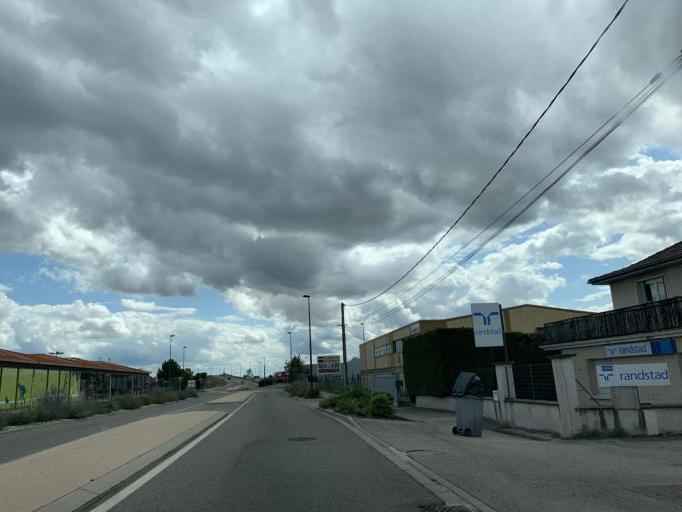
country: FR
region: Rhone-Alpes
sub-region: Departement de l'Ain
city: Montluel
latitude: 45.8471
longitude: 5.0660
